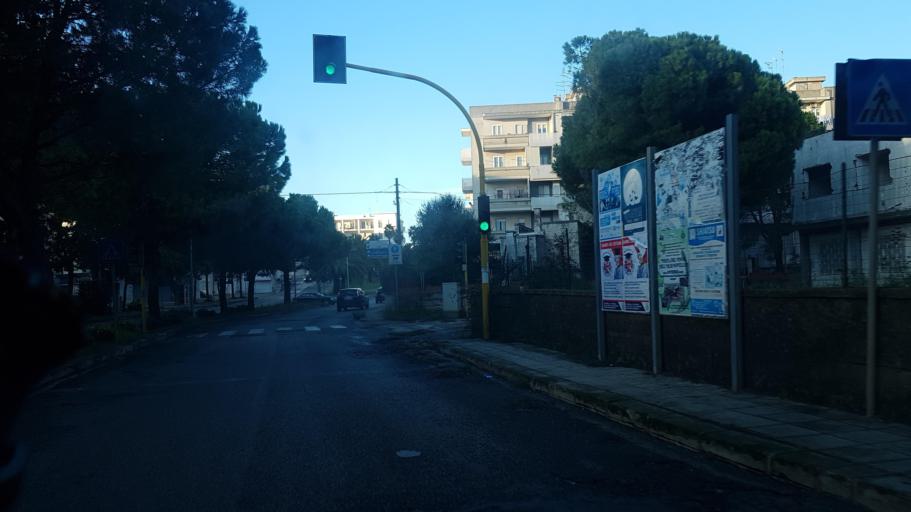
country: IT
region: Apulia
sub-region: Provincia di Brindisi
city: Ostuni
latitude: 40.7263
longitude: 17.5709
